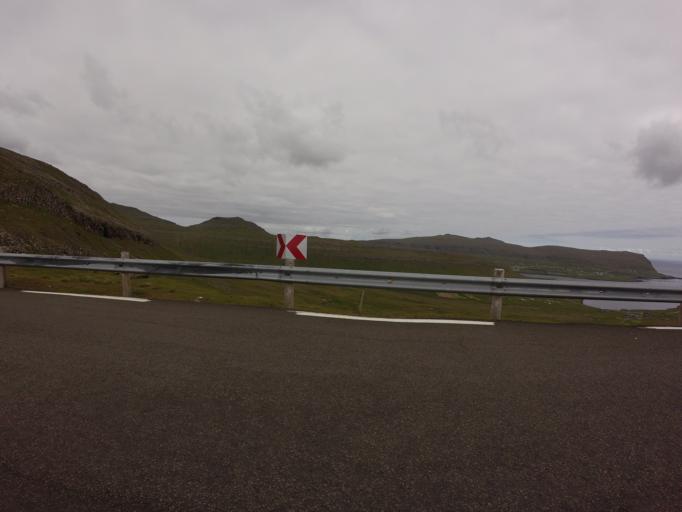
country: FO
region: Suduroy
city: Tvoroyri
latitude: 61.5250
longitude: -6.8376
